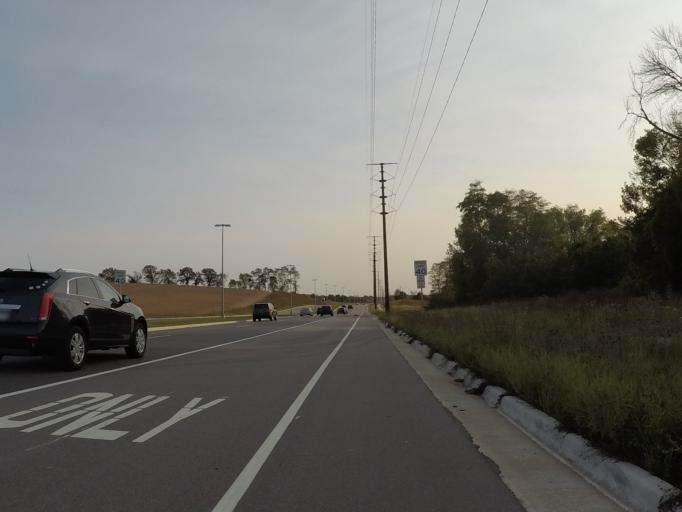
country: US
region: Wisconsin
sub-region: Dane County
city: Verona
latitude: 43.0425
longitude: -89.5331
